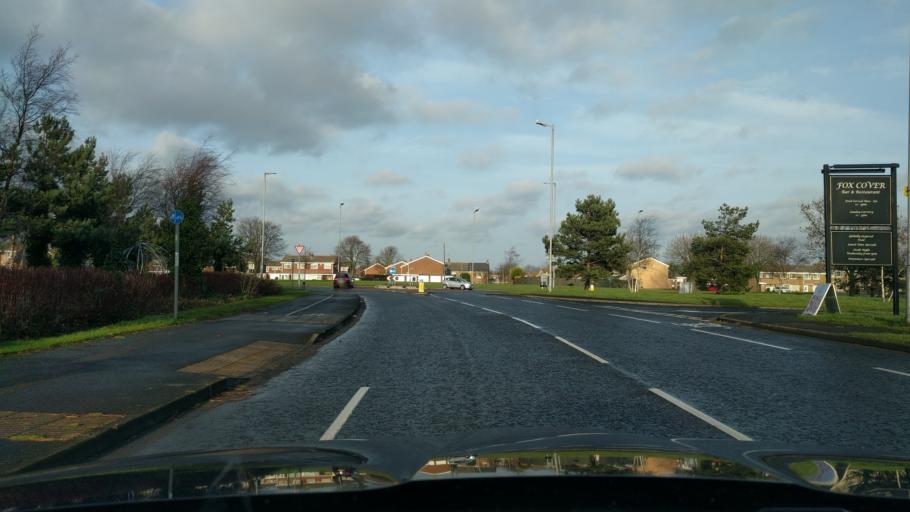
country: GB
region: England
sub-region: Northumberland
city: Newbiggin-by-the-Sea
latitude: 55.1700
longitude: -1.5490
